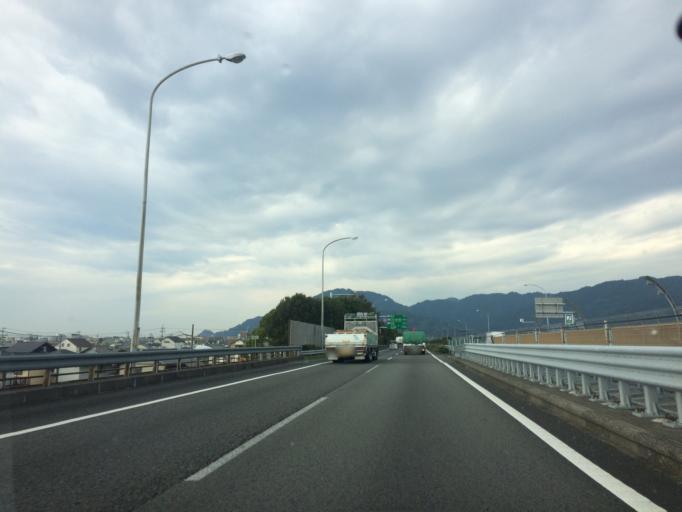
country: JP
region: Shizuoka
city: Shizuoka-shi
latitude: 34.9406
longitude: 138.3829
